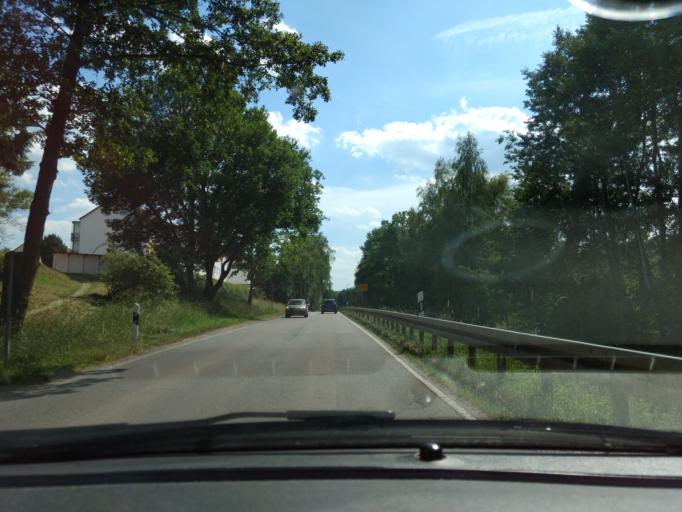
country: DE
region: Saxony
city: Dippoldiswalde
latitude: 50.9046
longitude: 13.6667
